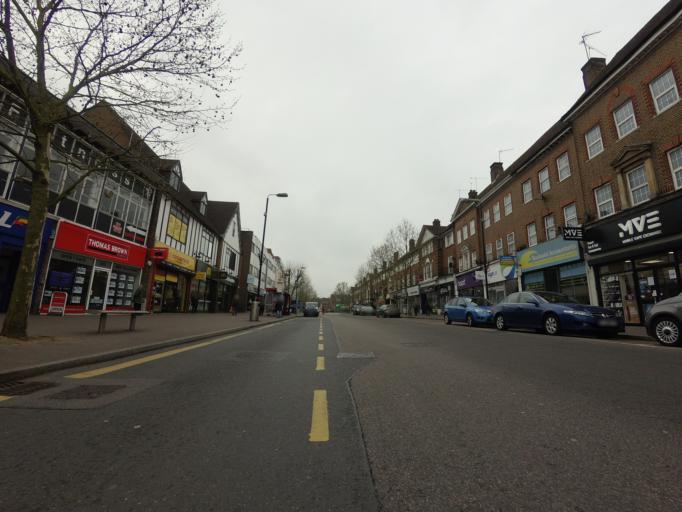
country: GB
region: England
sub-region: Greater London
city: Orpington
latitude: 51.3744
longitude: 0.0984
